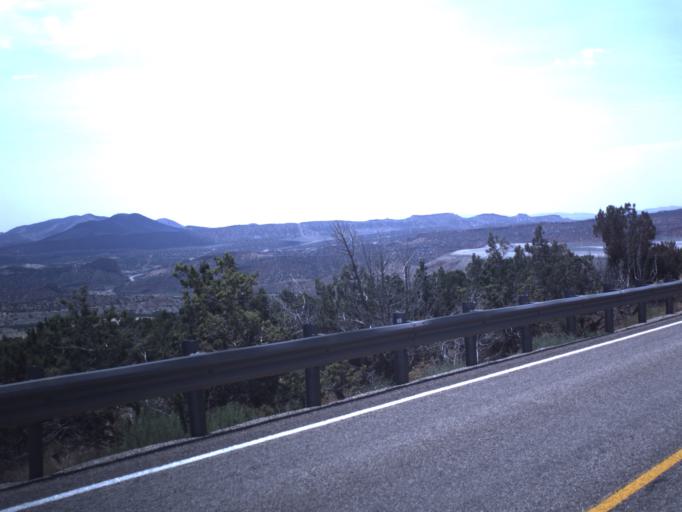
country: US
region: Utah
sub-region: Uintah County
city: Vernal
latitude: 40.6182
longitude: -109.4735
